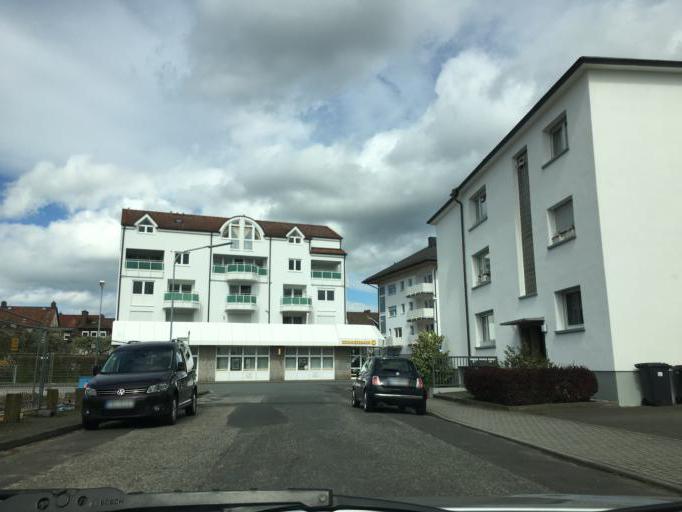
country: DE
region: Hesse
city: Obertshausen
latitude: 50.0696
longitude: 8.8449
